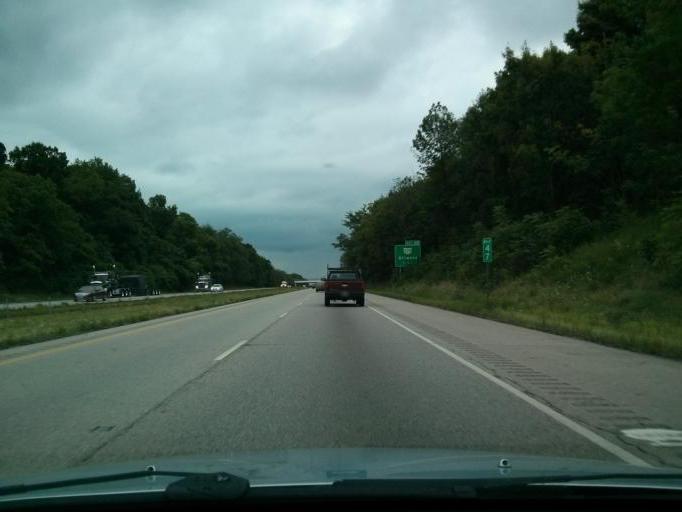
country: US
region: Ohio
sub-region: Mahoning County
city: Craig Beach
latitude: 41.1059
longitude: -81.0769
